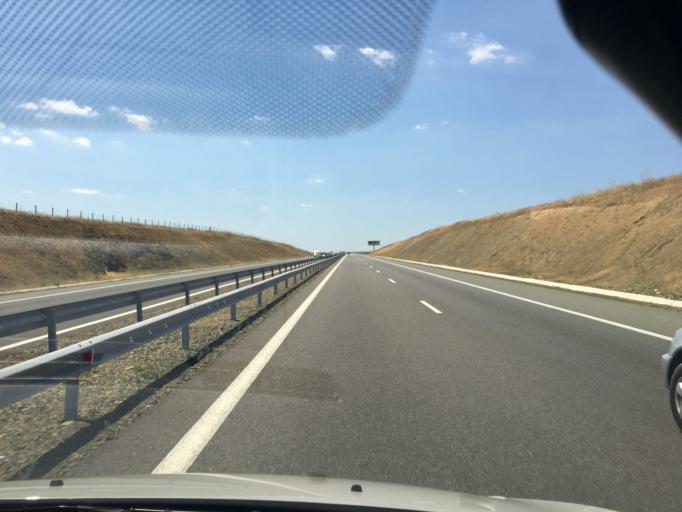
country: BG
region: Burgas
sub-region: Obshtina Karnobat
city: Karnobat
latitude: 42.5886
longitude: 26.9594
